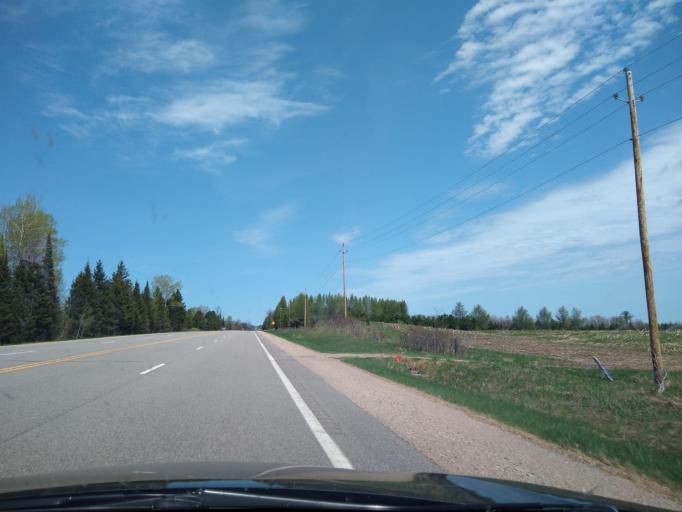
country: US
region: Michigan
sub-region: Delta County
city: Gladstone
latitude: 46.0920
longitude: -86.9807
